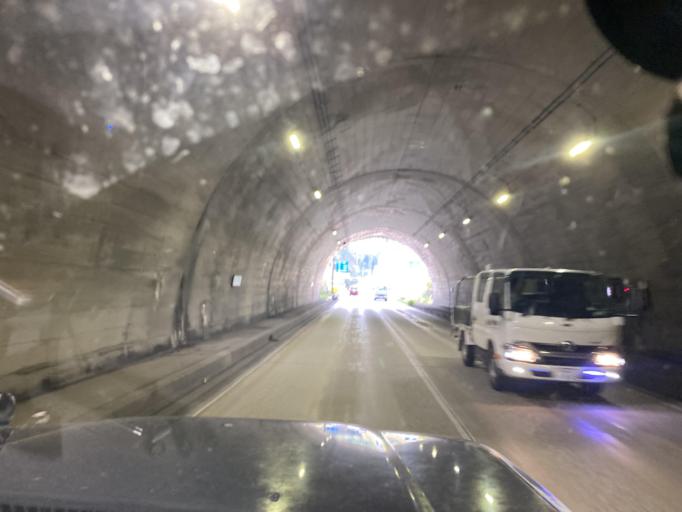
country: JP
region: Nagano
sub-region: Kitaazumi Gun
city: Hakuba
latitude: 36.6222
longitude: 137.8573
